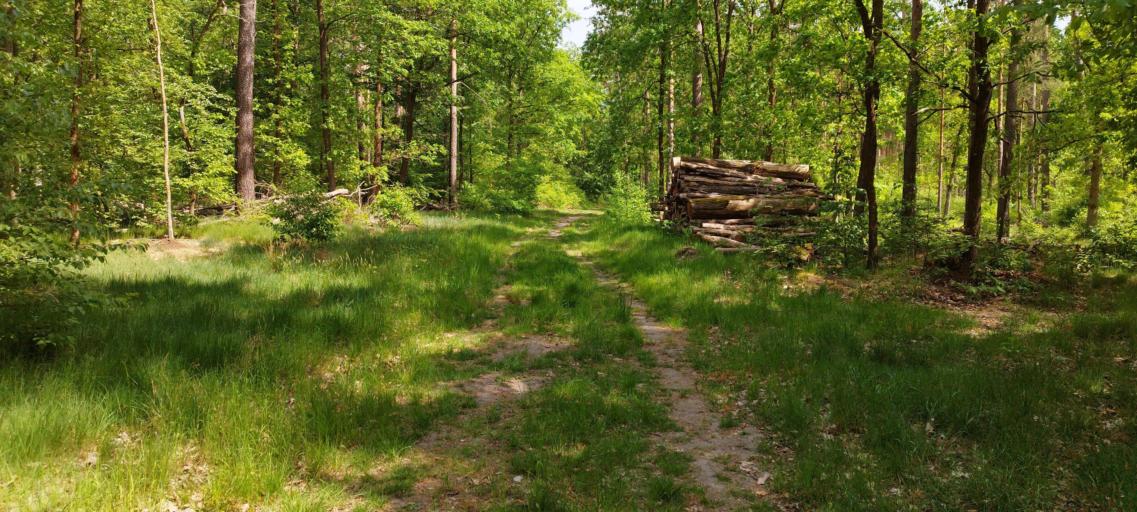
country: DE
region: Brandenburg
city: Rauen
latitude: 52.3665
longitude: 14.0227
